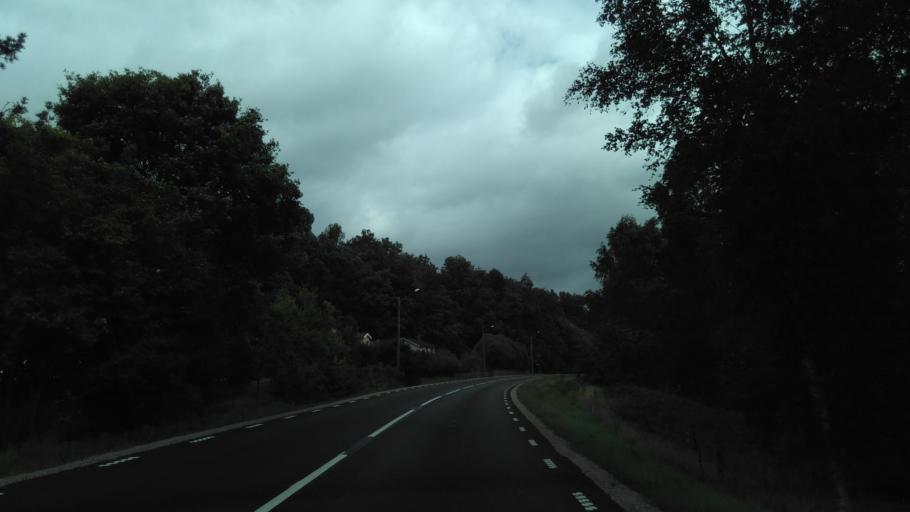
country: SE
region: Vaestra Goetaland
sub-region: Boras Kommun
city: Viskafors
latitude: 57.6103
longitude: 12.7947
